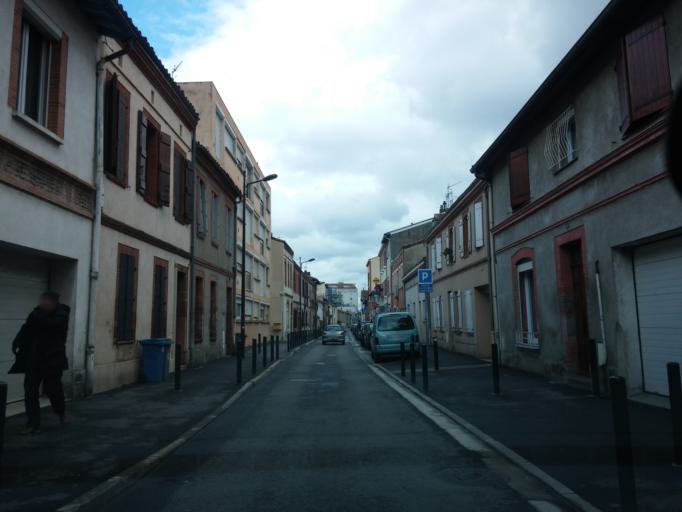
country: FR
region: Midi-Pyrenees
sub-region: Departement de la Haute-Garonne
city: Toulouse
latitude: 43.6016
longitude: 1.4166
